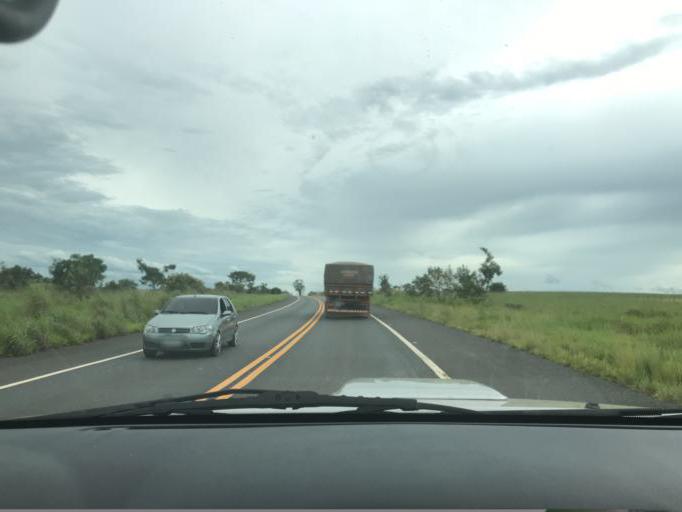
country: BR
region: Minas Gerais
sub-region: Araxa
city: Araxa
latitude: -19.3670
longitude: -46.8544
